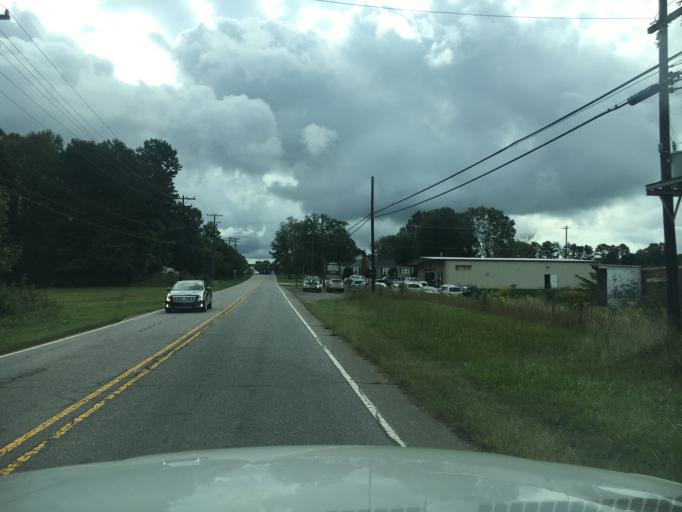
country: US
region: North Carolina
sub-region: Catawba County
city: Saint Stephens
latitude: 35.7250
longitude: -81.2673
